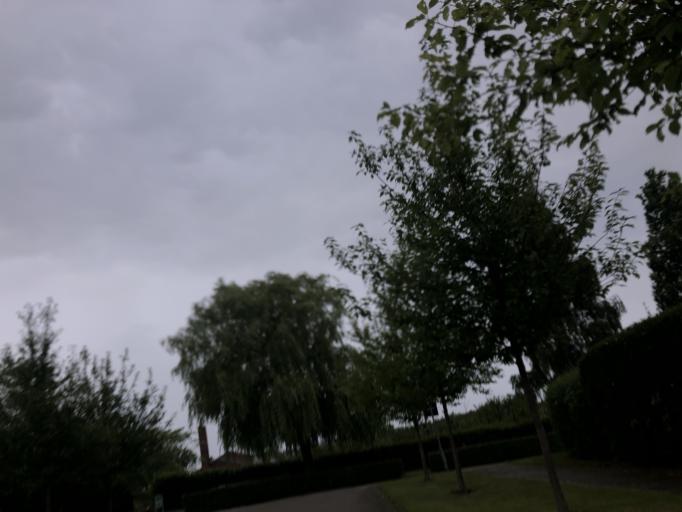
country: DK
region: Capital Region
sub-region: Gladsaxe Municipality
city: Buddinge
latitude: 55.7493
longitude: 12.4892
